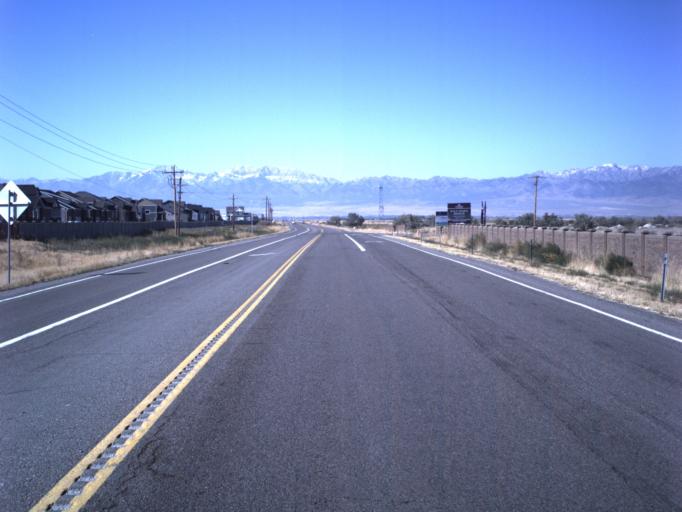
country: US
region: Utah
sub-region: Tooele County
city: Stansbury park
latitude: 40.6440
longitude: -112.3105
